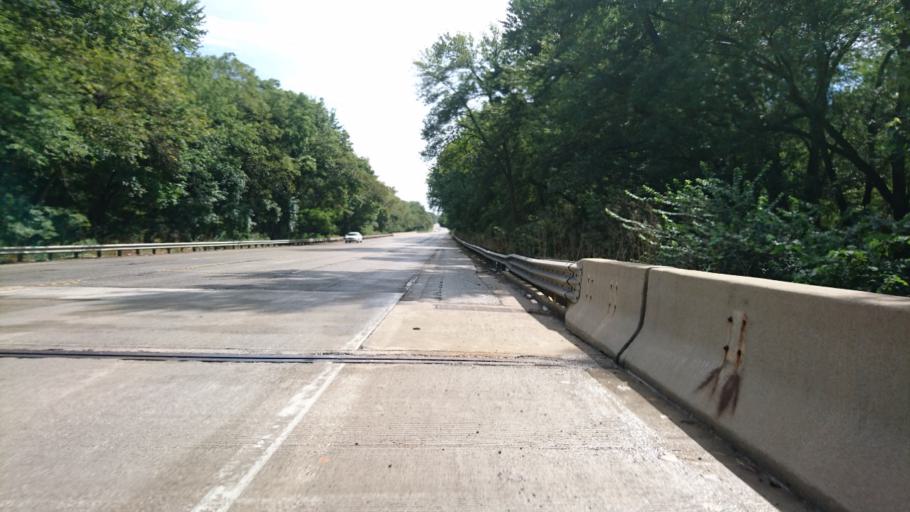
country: US
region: Illinois
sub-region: Sangamon County
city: Sherman
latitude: 39.8698
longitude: -89.6141
